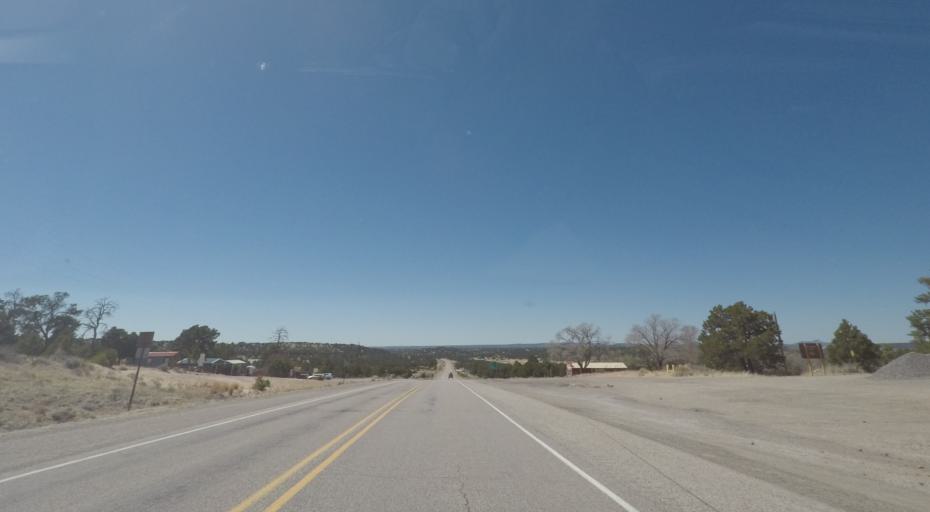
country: US
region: New Mexico
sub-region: Socorro County
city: Alamo
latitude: 34.2997
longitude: -108.1331
